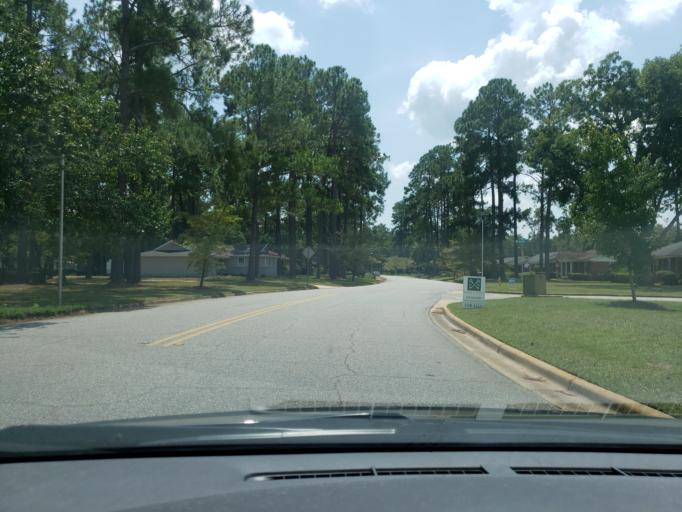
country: US
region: Georgia
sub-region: Dougherty County
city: Albany
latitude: 31.6018
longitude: -84.2050
